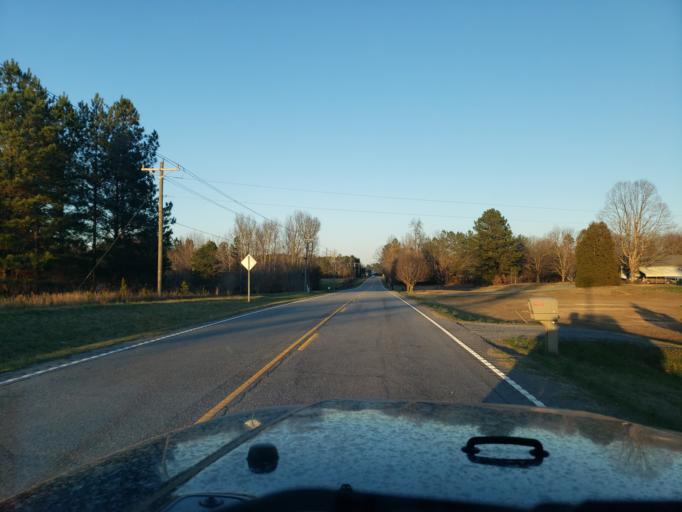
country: US
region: South Carolina
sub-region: York County
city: Clover
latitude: 35.1128
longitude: -81.3127
